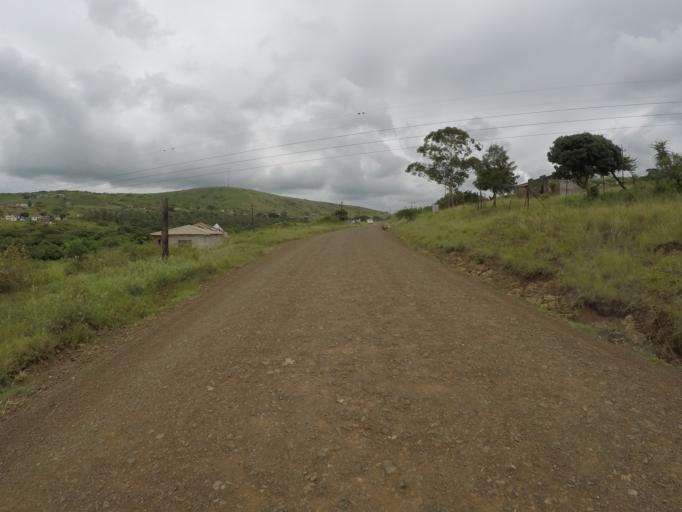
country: ZA
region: KwaZulu-Natal
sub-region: uThungulu District Municipality
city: Empangeni
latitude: -28.7091
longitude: 31.8491
